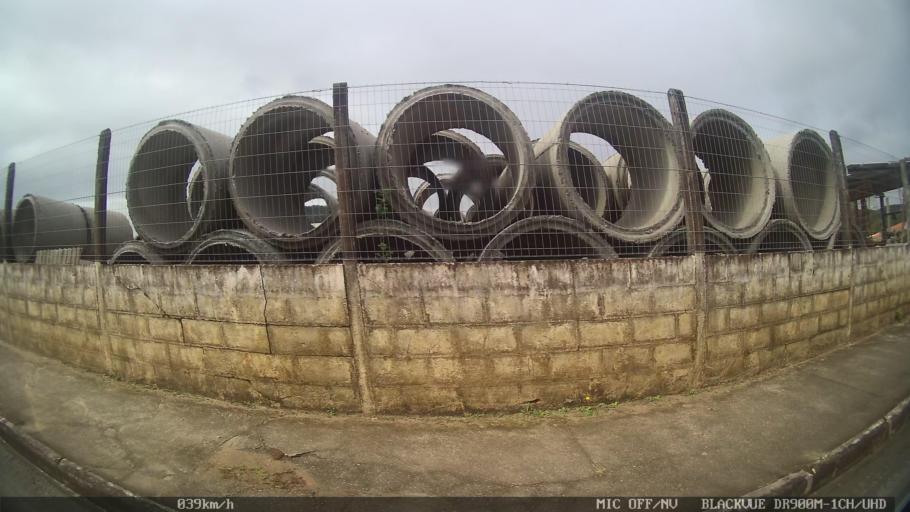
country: BR
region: Santa Catarina
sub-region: Biguacu
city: Biguacu
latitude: -27.5189
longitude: -48.6569
